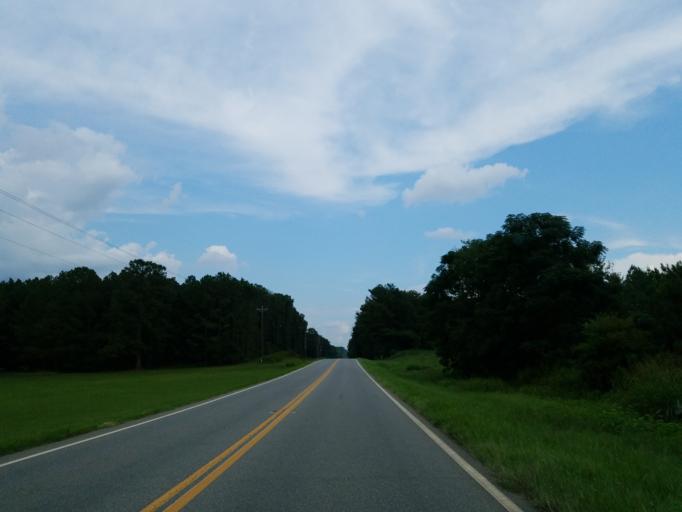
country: US
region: Georgia
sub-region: Dooly County
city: Unadilla
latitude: 32.3293
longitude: -83.7406
